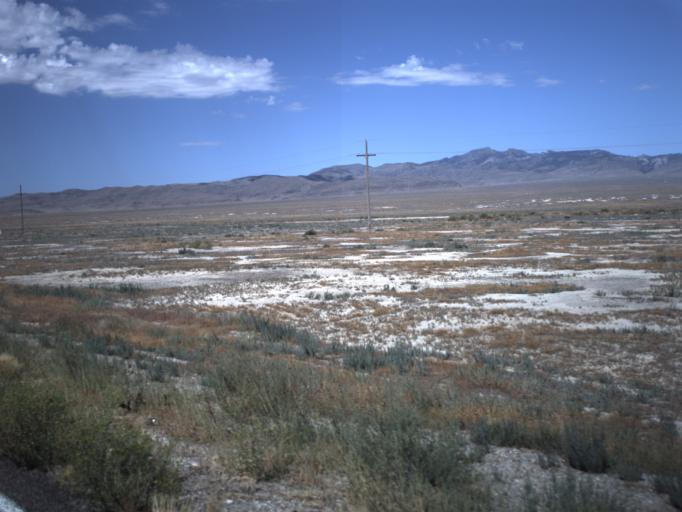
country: US
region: Utah
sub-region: Millard County
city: Delta
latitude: 39.0924
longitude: -113.1684
